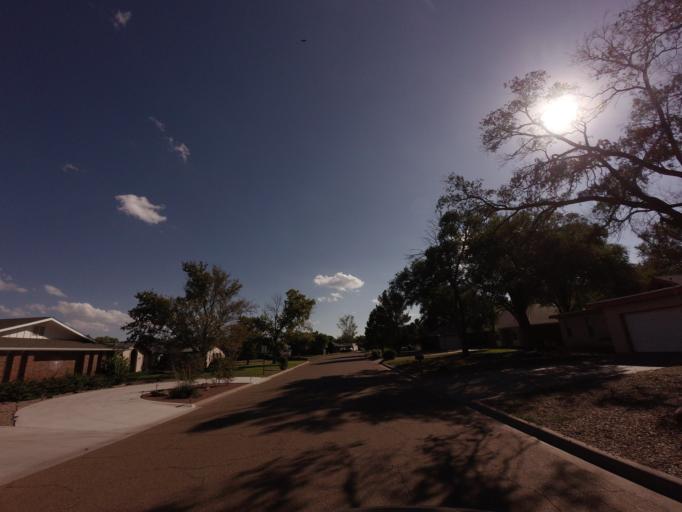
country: US
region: New Mexico
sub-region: Curry County
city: Clovis
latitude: 34.4393
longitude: -103.1811
